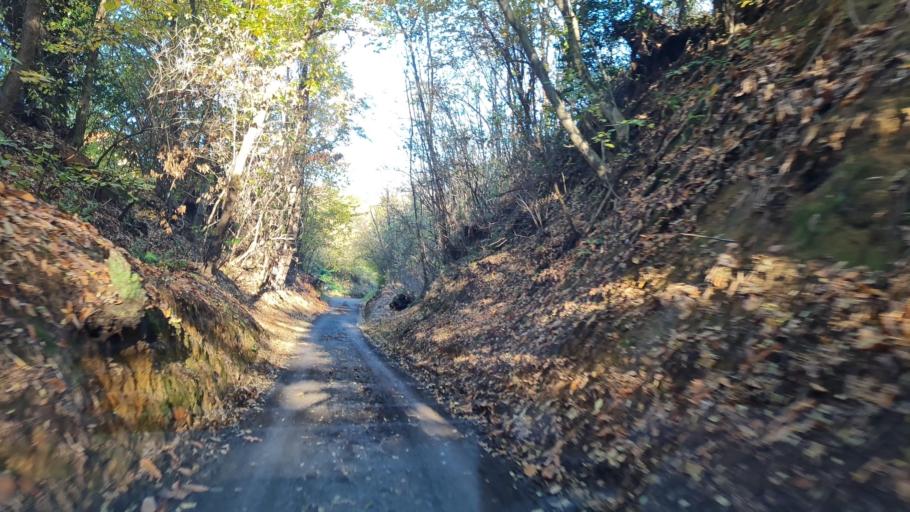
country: IT
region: Piedmont
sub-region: Provincia di Biella
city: Masserano
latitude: 45.5811
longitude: 8.2294
